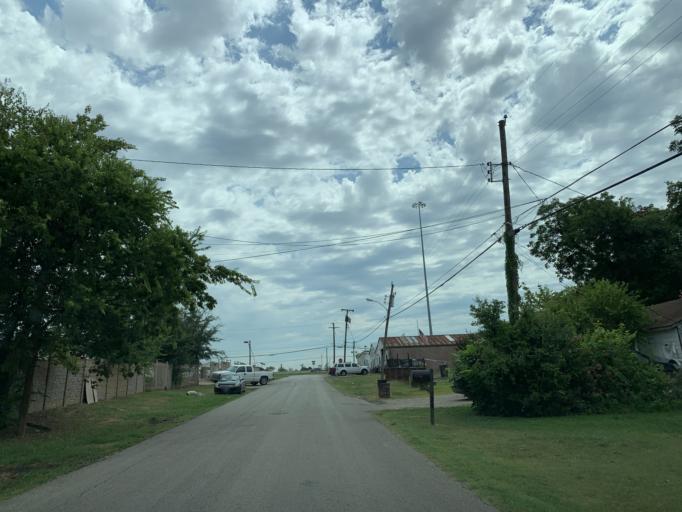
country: US
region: Texas
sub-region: Dallas County
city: Duncanville
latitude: 32.6713
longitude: -96.8244
